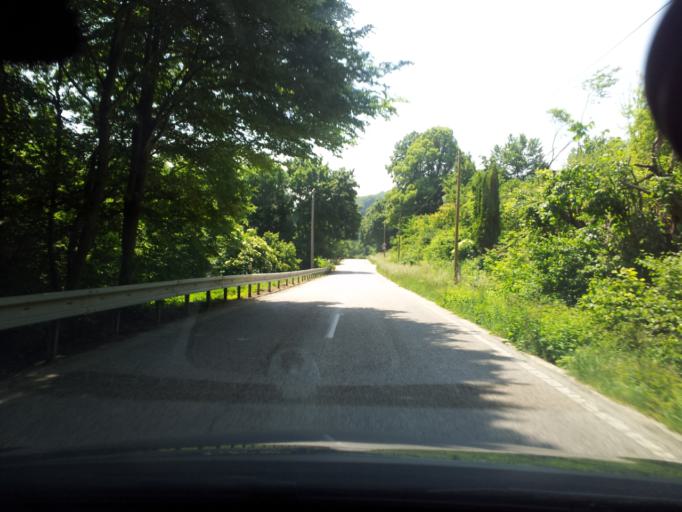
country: SK
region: Nitriansky
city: Partizanske
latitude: 48.5843
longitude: 18.4531
